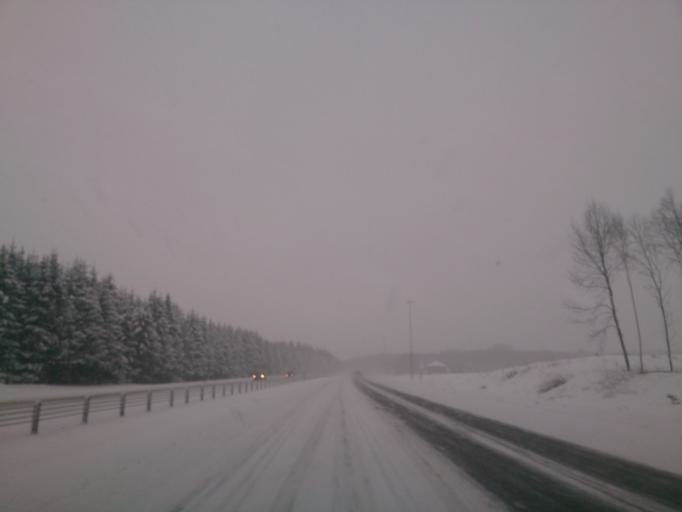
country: SE
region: Soedermanland
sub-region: Nykopings Kommun
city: Svalsta
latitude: 58.7485
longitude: 16.9221
